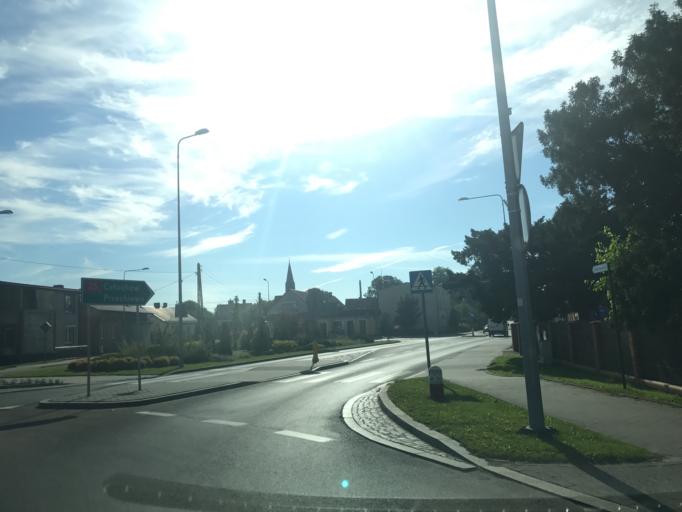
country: PL
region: Pomeranian Voivodeship
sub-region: Powiat czluchowski
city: Rzeczenica
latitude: 53.7576
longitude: 17.1077
